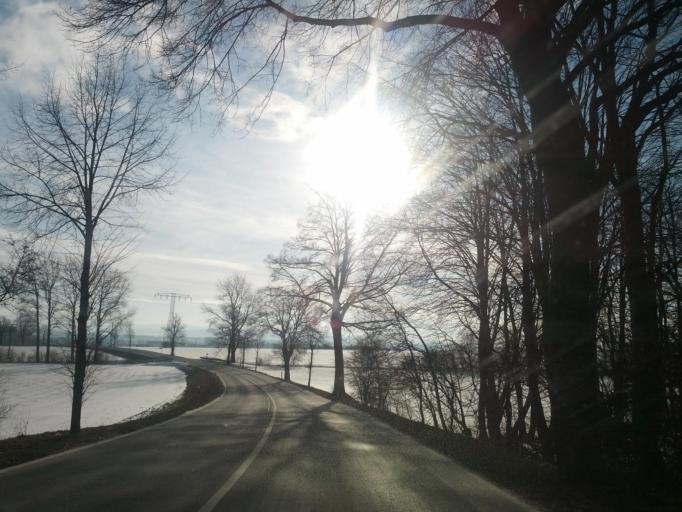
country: DE
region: Thuringia
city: Friedrichswerth
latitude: 51.0392
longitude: 10.5314
